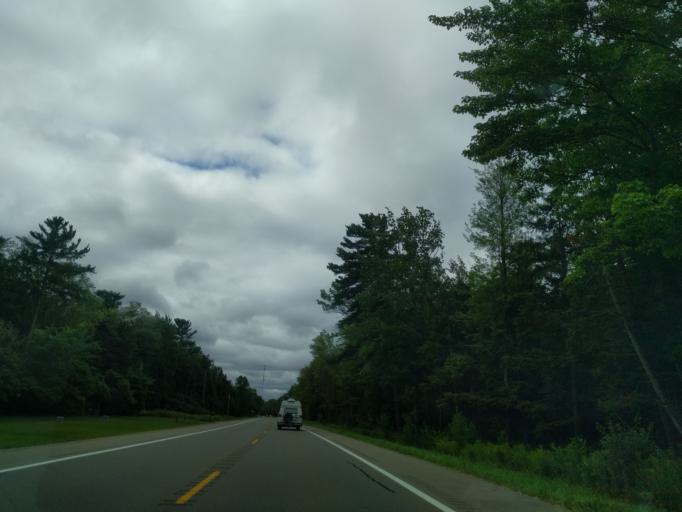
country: US
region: Michigan
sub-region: Menominee County
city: Menominee
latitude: 45.2772
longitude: -87.4630
